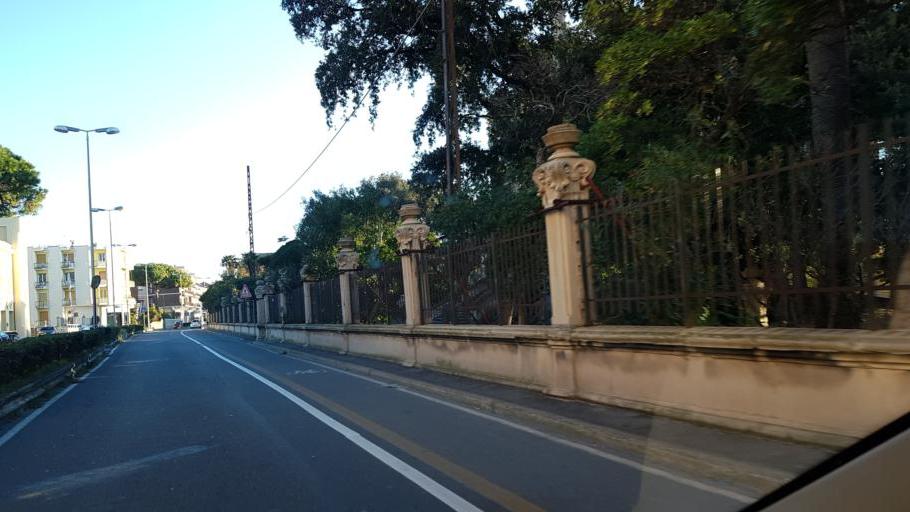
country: IT
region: Liguria
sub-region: Provincia di Savona
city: Savona
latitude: 44.2928
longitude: 8.4558
